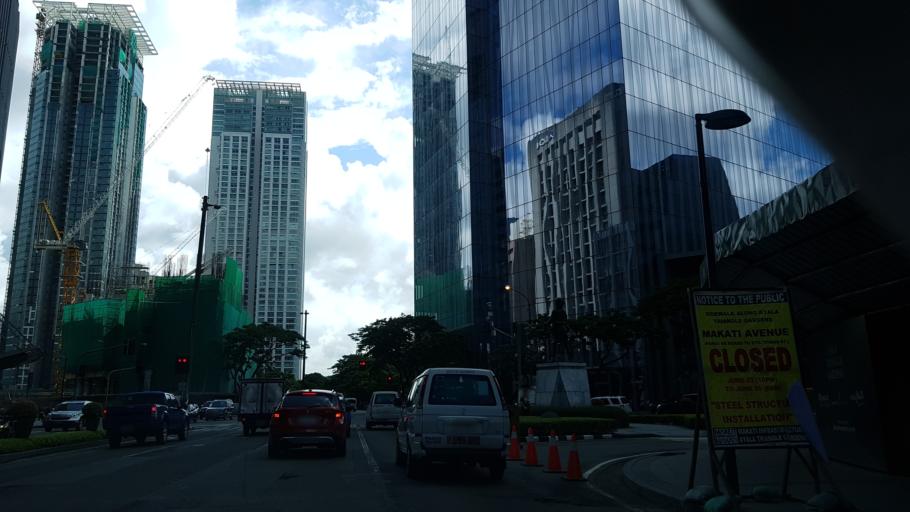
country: PH
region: Metro Manila
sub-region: Makati City
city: Makati City
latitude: 14.5580
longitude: 121.0255
